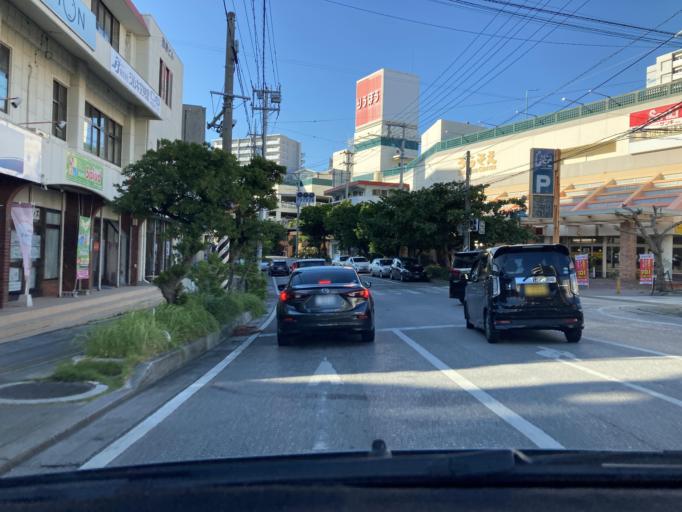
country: JP
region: Okinawa
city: Ginowan
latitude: 26.2578
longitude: 127.7130
